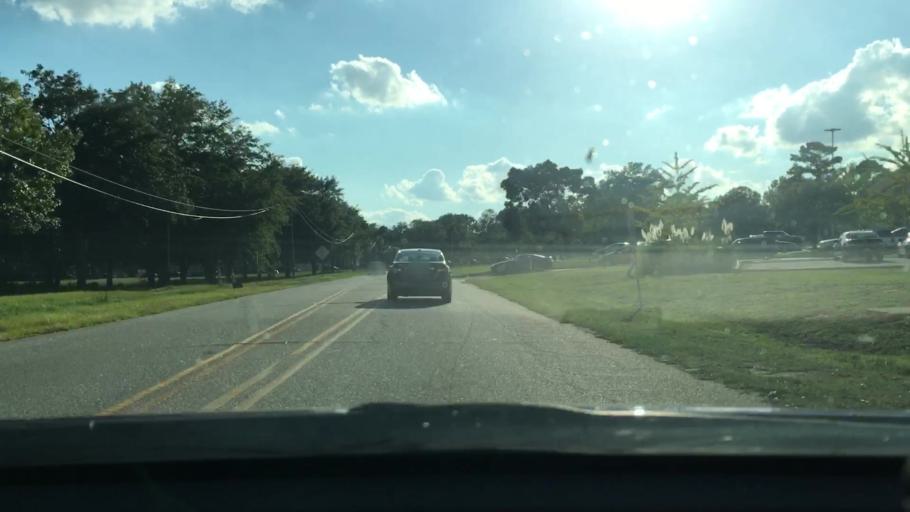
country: US
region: South Carolina
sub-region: Richland County
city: Columbia
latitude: 34.0206
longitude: -81.0340
